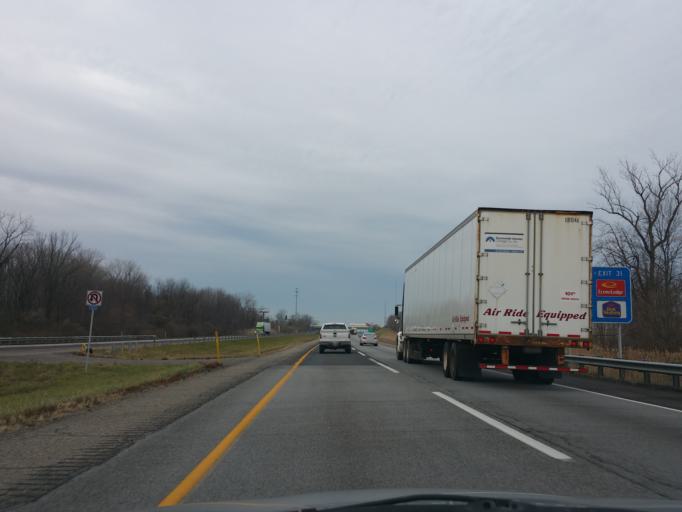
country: US
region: Indiana
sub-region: Porter County
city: Chesterton
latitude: 41.5724
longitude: -87.0371
